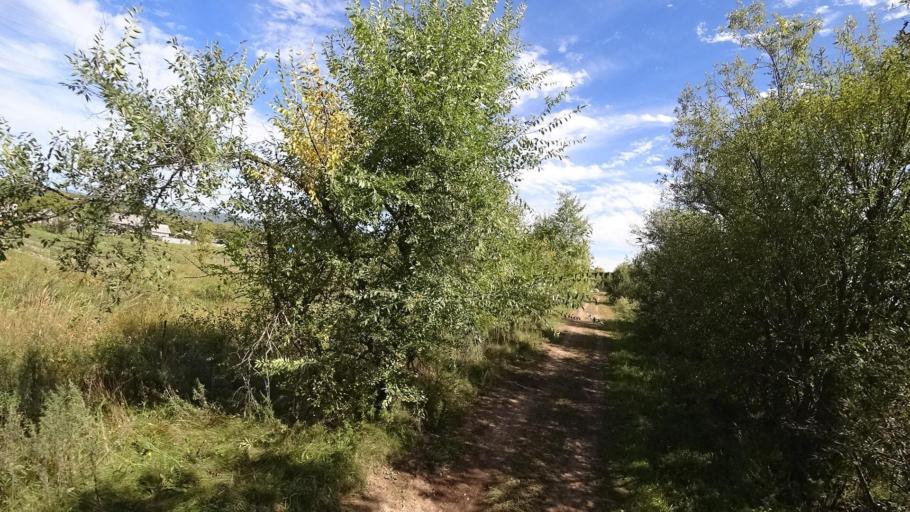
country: RU
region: Primorskiy
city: Yakovlevka
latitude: 44.4301
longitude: 133.5717
